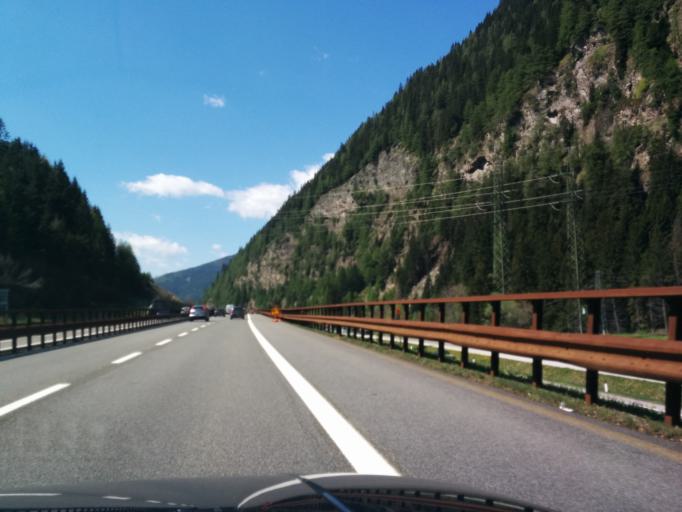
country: IT
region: Trentino-Alto Adige
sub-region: Bolzano
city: Colle Isarco
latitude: 46.9660
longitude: 11.4674
